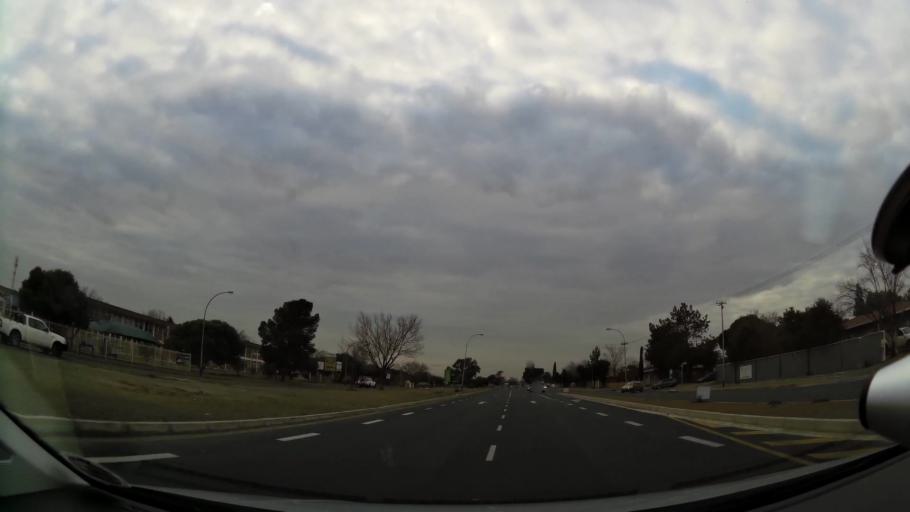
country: ZA
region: Orange Free State
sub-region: Mangaung Metropolitan Municipality
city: Bloemfontein
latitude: -29.1258
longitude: 26.1901
